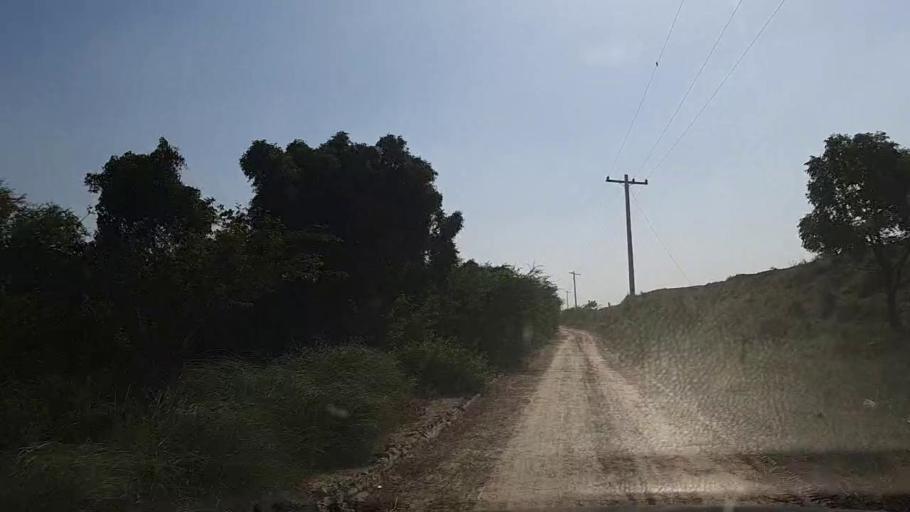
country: PK
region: Sindh
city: Daro Mehar
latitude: 24.7776
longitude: 68.0690
